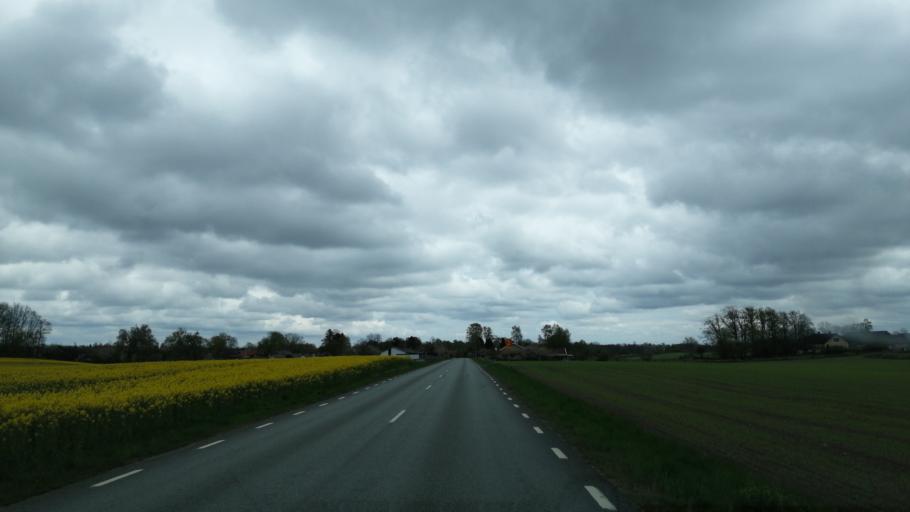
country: SE
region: Skane
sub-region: Kristianstads Kommun
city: Onnestad
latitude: 55.9931
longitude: 14.0267
